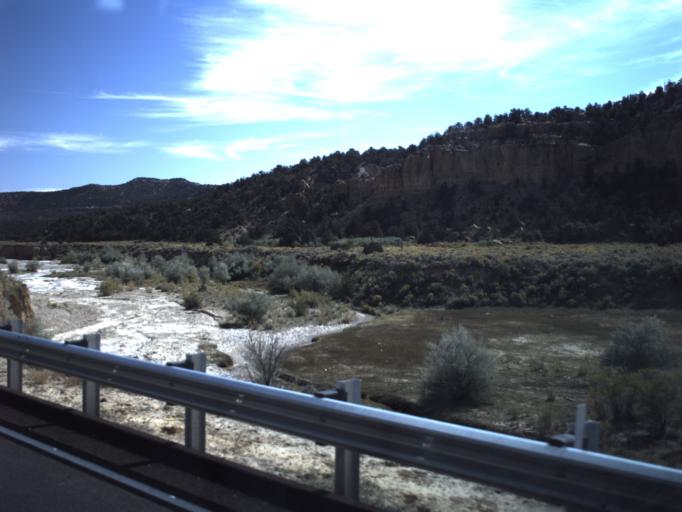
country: US
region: Utah
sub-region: Wayne County
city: Loa
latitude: 37.7359
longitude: -111.7486
